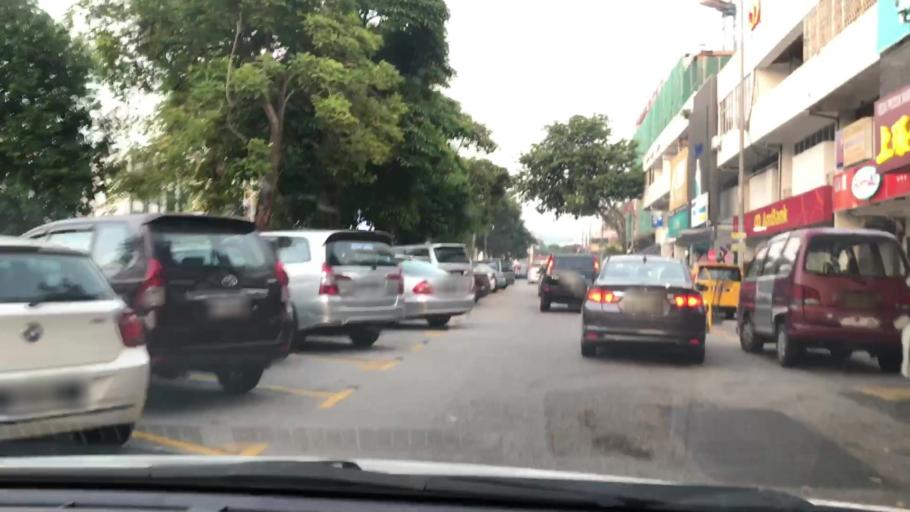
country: MY
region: Selangor
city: Kampong Baharu Balakong
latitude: 3.0684
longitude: 101.6927
